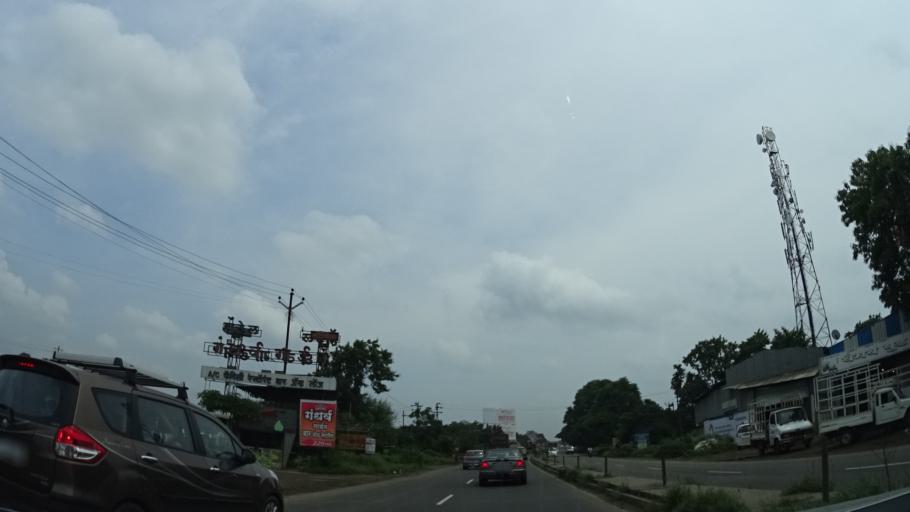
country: IN
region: Maharashtra
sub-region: Pune Division
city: Koregaon
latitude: 18.6553
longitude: 74.0797
